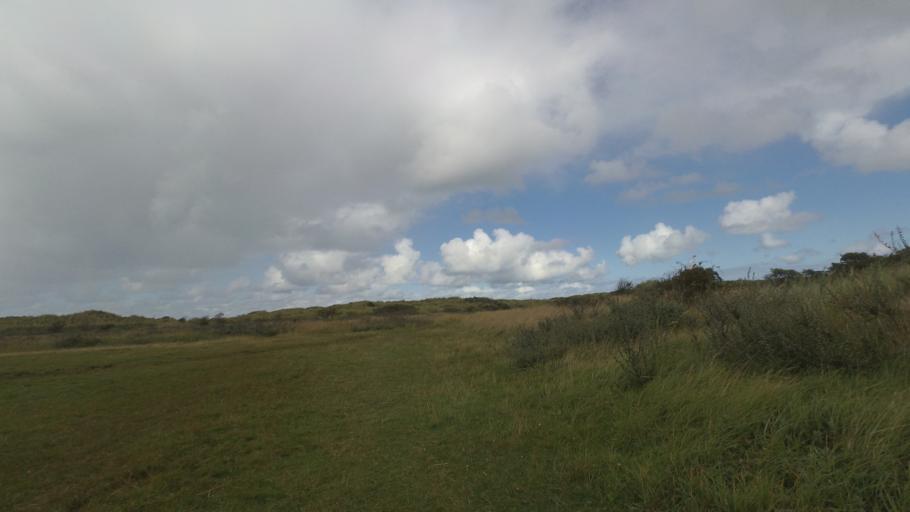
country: NL
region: Friesland
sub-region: Gemeente Ameland
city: Nes
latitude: 53.4544
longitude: 5.8378
